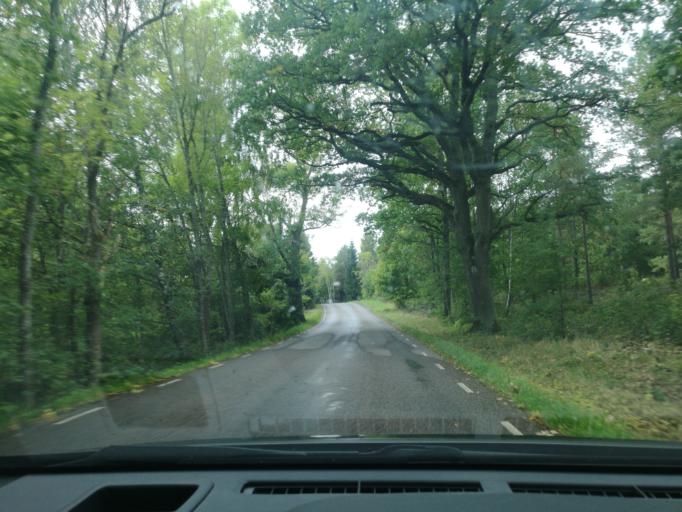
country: SE
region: OEstergoetland
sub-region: Soderkopings Kommun
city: Soederkoeping
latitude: 58.5298
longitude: 16.2964
